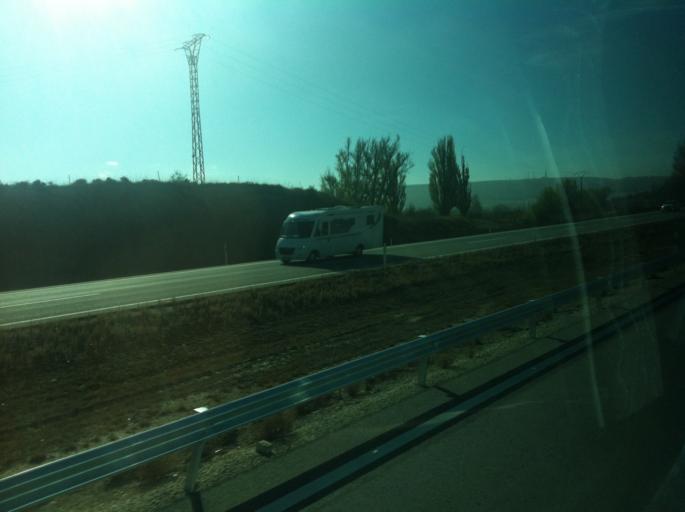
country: ES
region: Castille and Leon
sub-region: Provincia de Burgos
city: Quintanapalla
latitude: 42.4148
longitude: -3.5267
